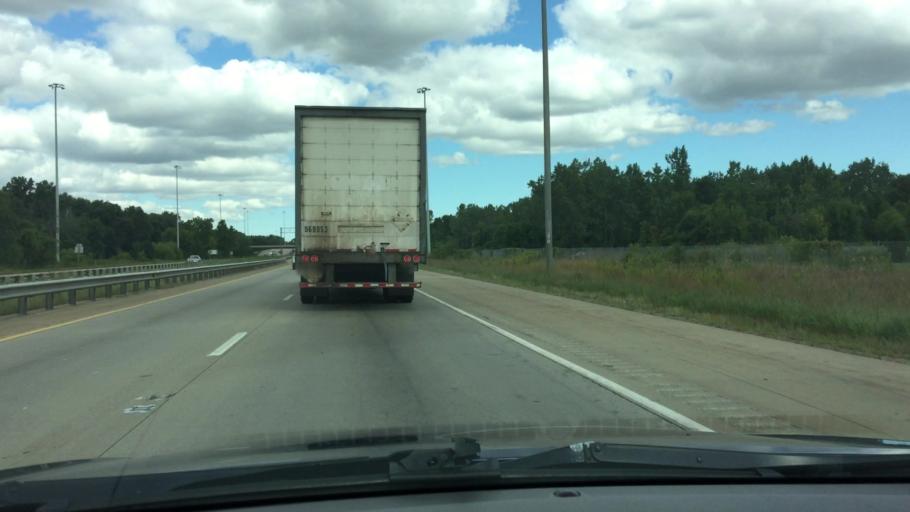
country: US
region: Illinois
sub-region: Cook County
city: Thornton
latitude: 41.5650
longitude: -87.5835
